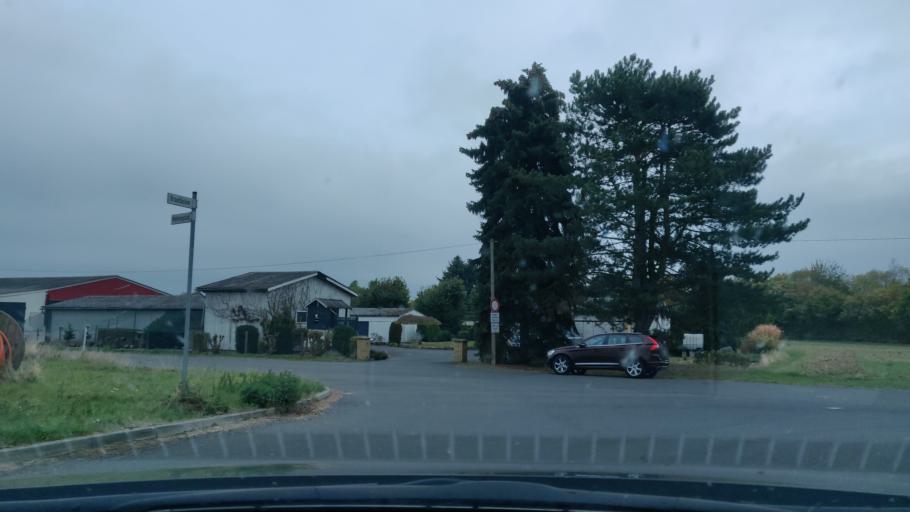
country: DE
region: Hesse
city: Fritzlar
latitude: 51.1408
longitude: 9.2803
